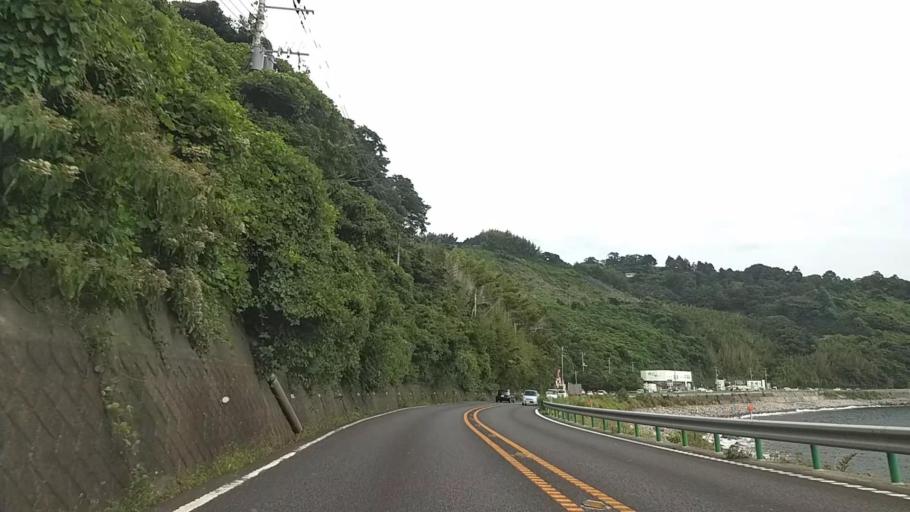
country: JP
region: Kanagawa
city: Yugawara
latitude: 35.1809
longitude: 139.1360
